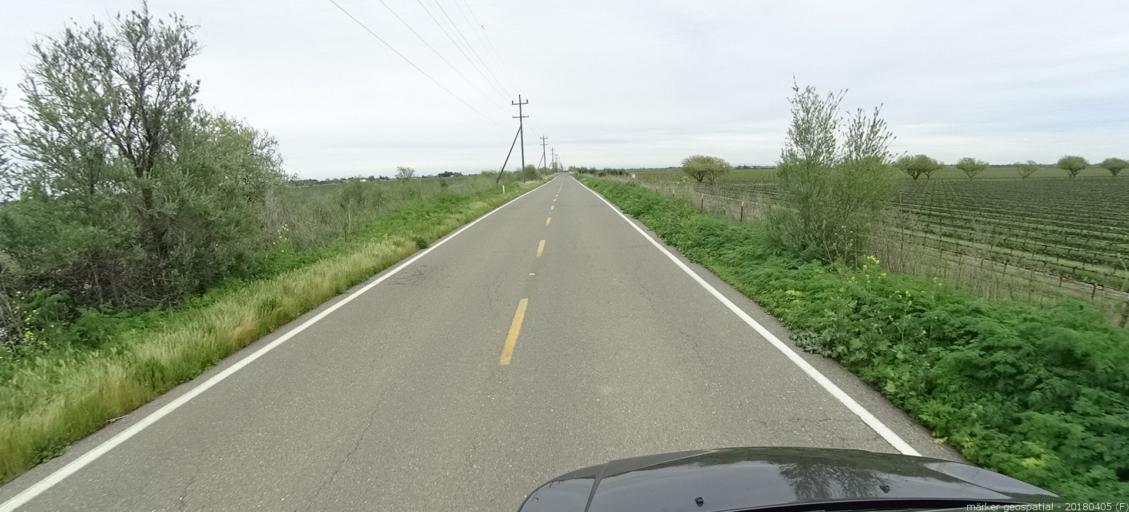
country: US
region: California
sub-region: Sacramento County
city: Walnut Grove
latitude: 38.3205
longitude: -121.4887
